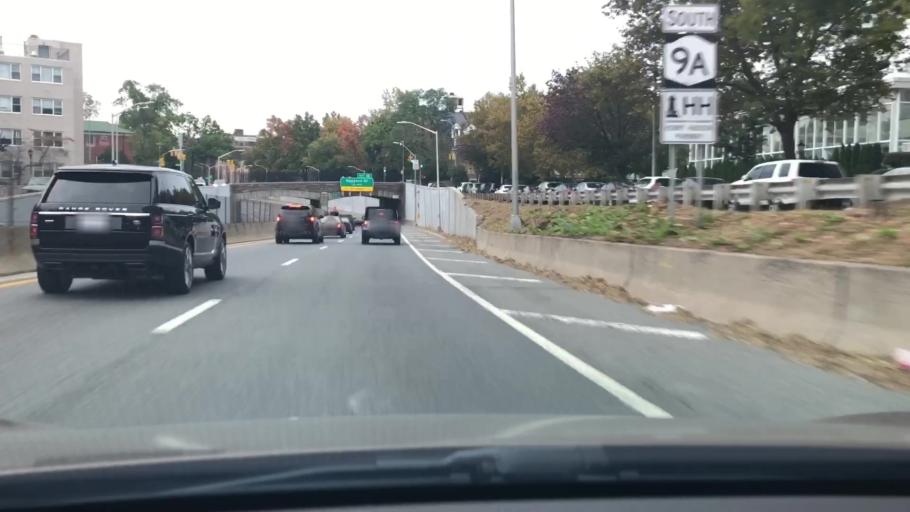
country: US
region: New York
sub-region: New York County
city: Inwood
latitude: 40.8854
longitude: -73.9138
